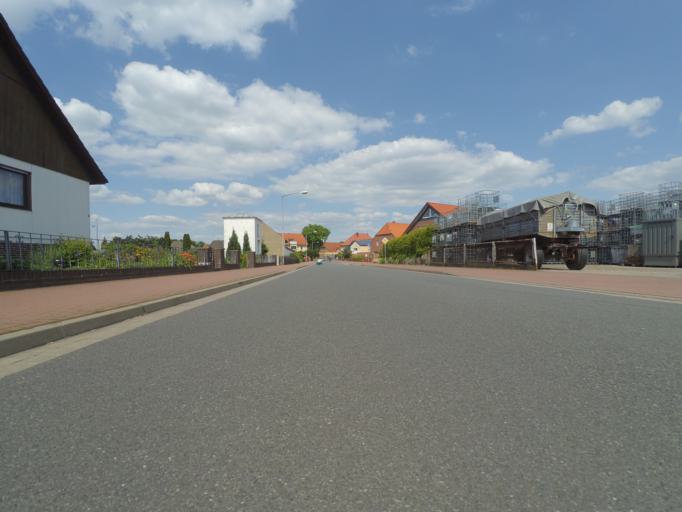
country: DE
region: Lower Saxony
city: Uetze
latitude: 52.4630
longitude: 10.1980
